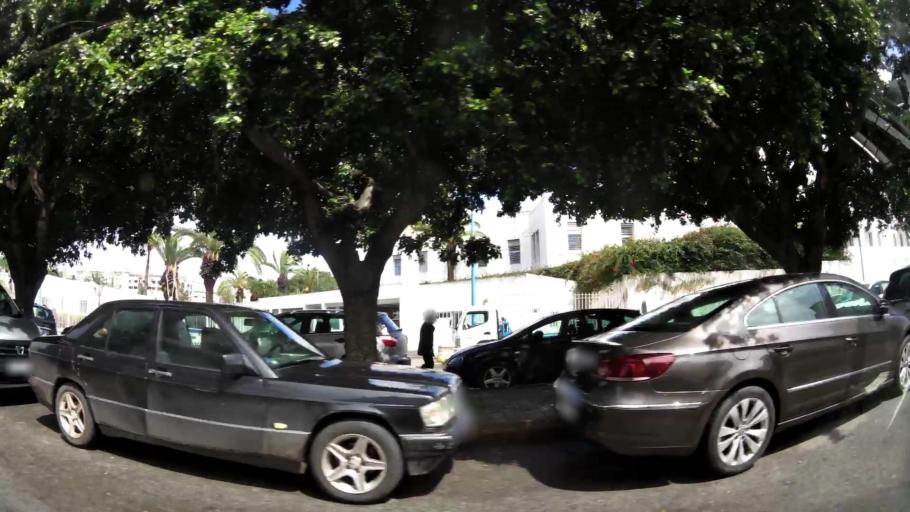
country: MA
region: Grand Casablanca
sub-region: Casablanca
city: Casablanca
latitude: 33.5806
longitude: -7.6217
